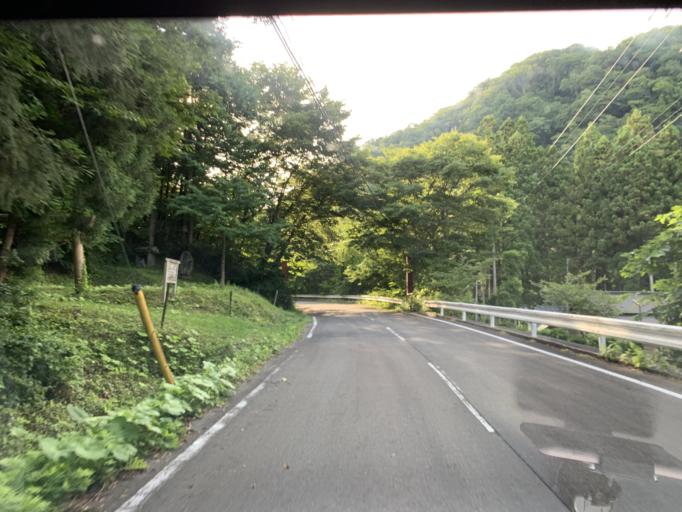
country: JP
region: Iwate
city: Ichinoseki
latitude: 38.9032
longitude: 140.9286
